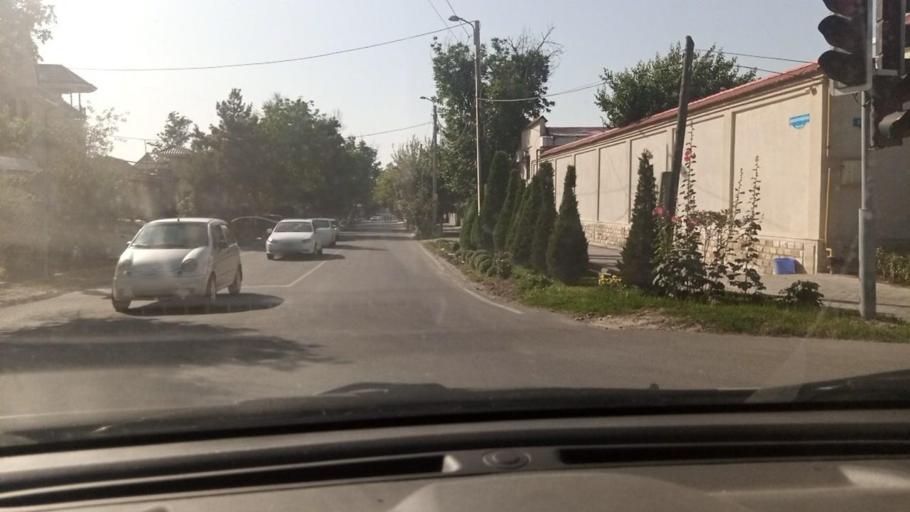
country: UZ
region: Toshkent
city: Salor
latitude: 41.3390
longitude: 69.3533
